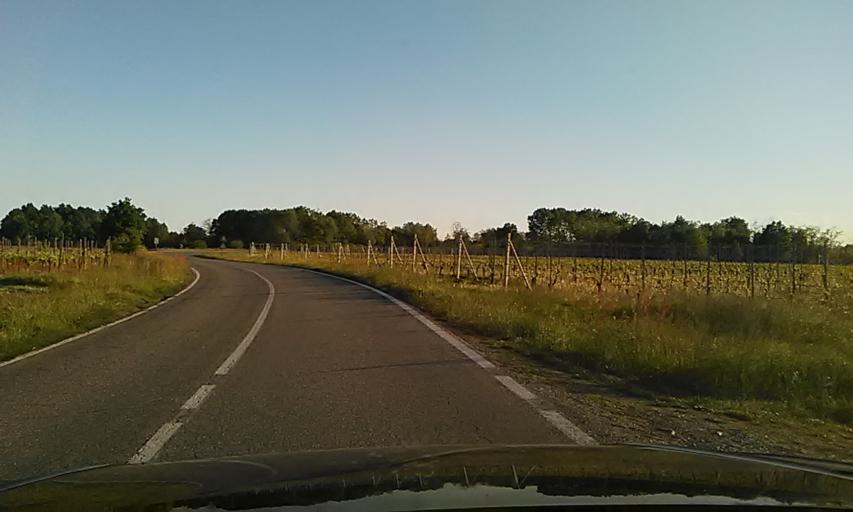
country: IT
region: Piedmont
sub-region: Provincia di Novara
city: Barengo
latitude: 45.5688
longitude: 8.5061
